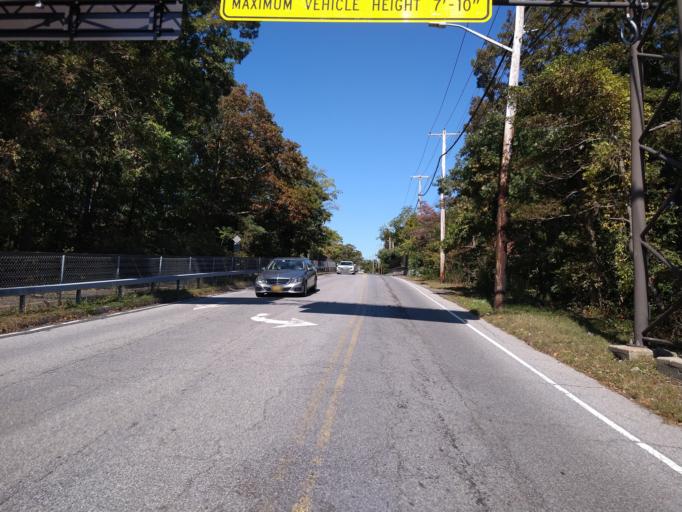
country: US
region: New York
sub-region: Nassau County
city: Plainview
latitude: 40.7980
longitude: -73.4678
